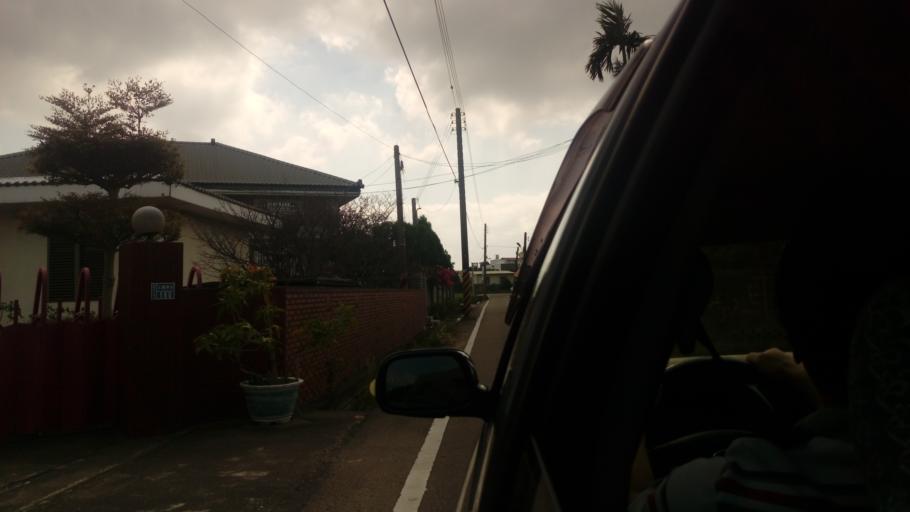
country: TW
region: Taiwan
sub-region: Miaoli
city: Miaoli
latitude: 24.5672
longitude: 120.8375
